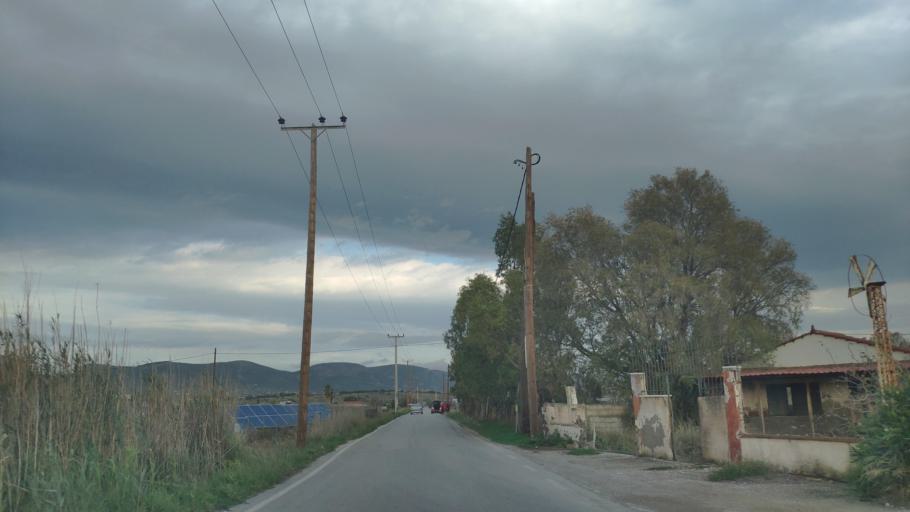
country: GR
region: Attica
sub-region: Nomarchia Dytikis Attikis
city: Nea Peramos
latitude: 37.9861
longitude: 23.3885
